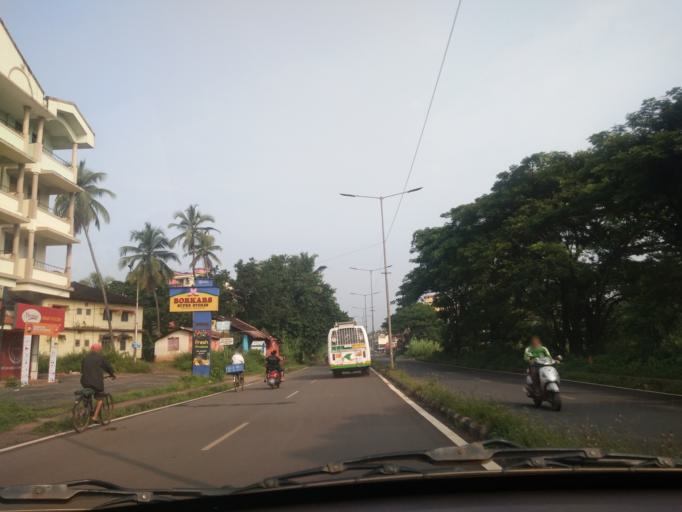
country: IN
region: Goa
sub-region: South Goa
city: Madgaon
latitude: 15.2598
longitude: 73.9646
